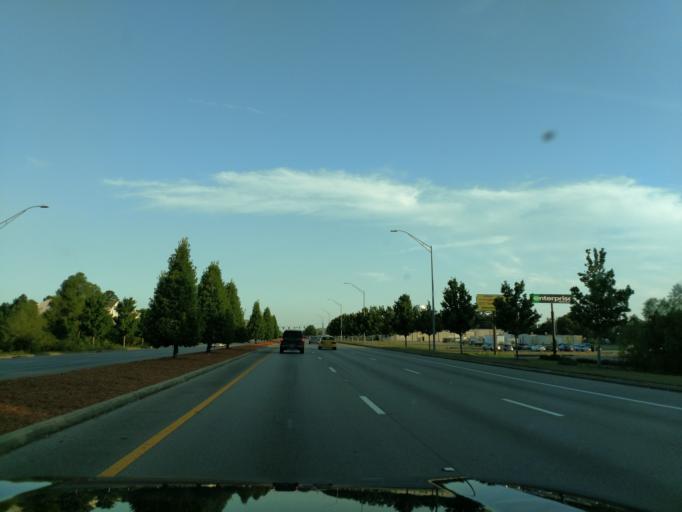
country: US
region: Mississippi
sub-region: Harrison County
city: West Gulfport
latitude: 30.4121
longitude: -89.0930
